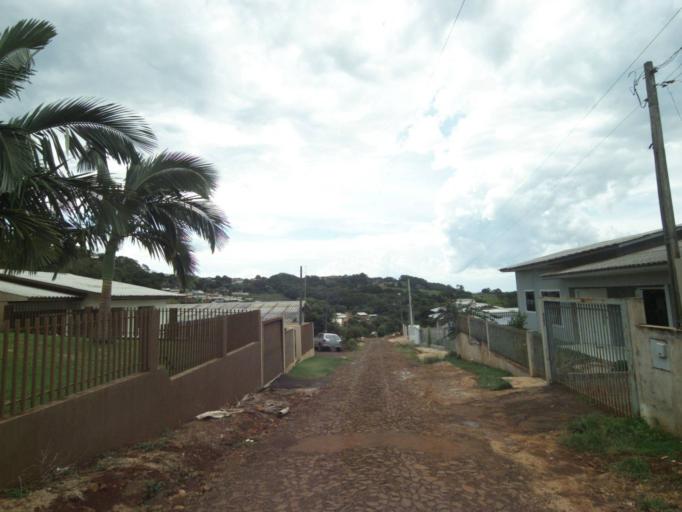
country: BR
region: Parana
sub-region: Guaraniacu
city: Guaraniacu
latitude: -25.0949
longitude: -52.8675
